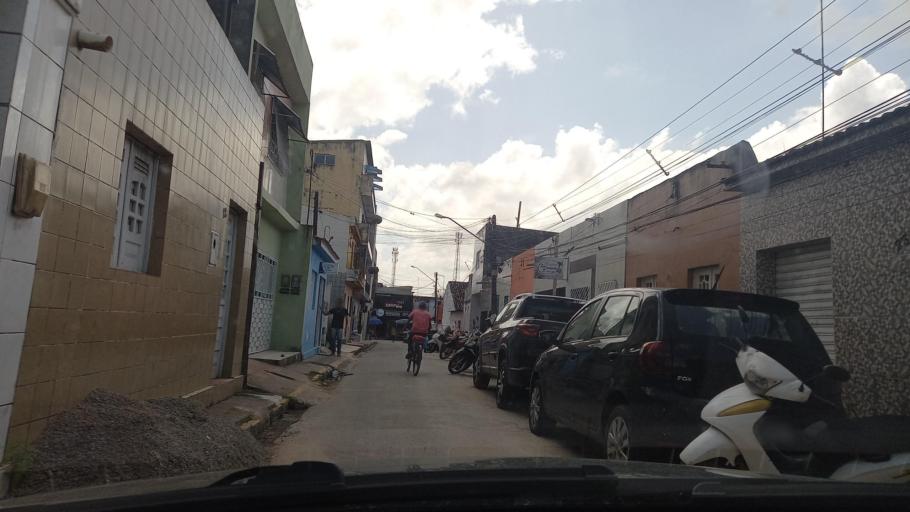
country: BR
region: Pernambuco
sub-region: Goiana
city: Goiana
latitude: -7.5614
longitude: -35.0003
